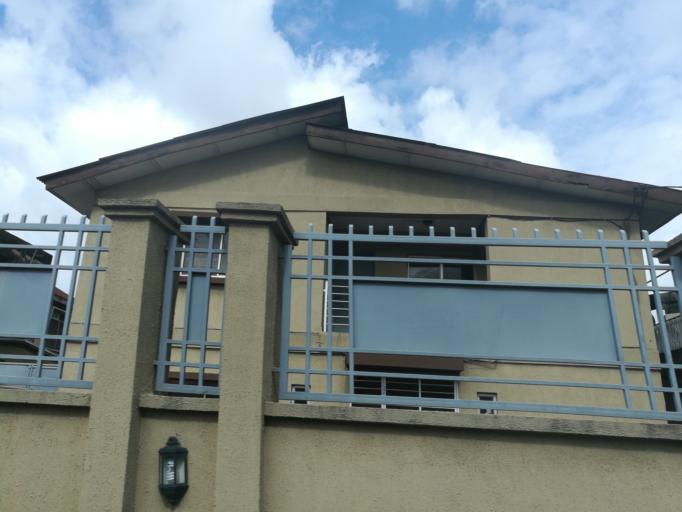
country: NG
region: Lagos
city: Somolu
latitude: 6.5483
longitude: 3.3690
